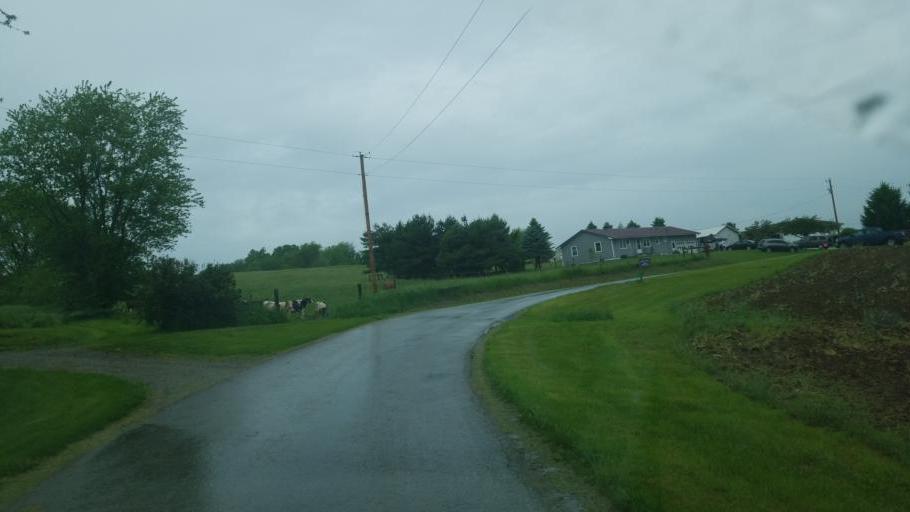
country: US
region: Ohio
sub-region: Wayne County
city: Apple Creek
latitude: 40.7430
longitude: -81.8632
